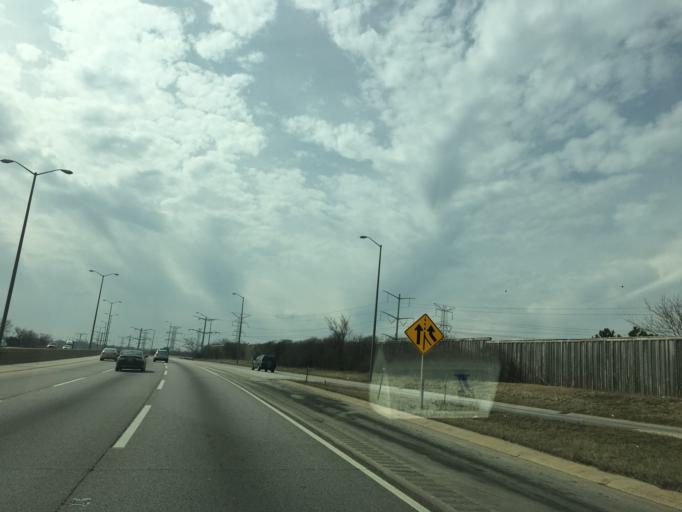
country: US
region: Illinois
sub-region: DuPage County
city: Lisle
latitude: 41.8059
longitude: -88.0549
